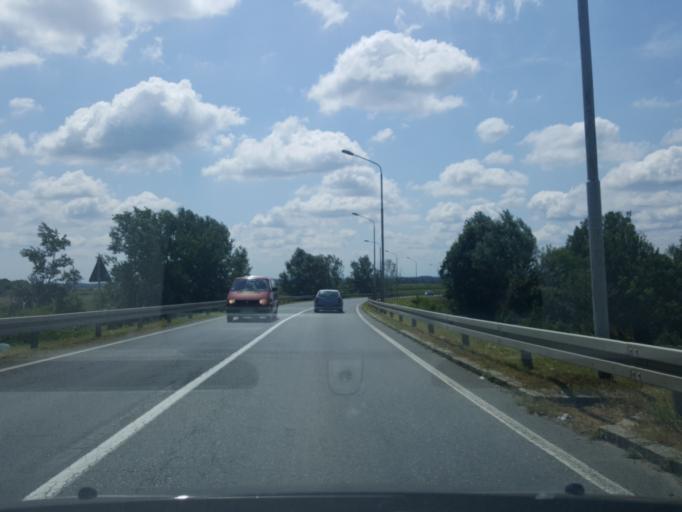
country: RS
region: Autonomna Pokrajina Vojvodina
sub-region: Sremski Okrug
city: Sremska Mitrovica
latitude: 44.9555
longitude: 19.6318
